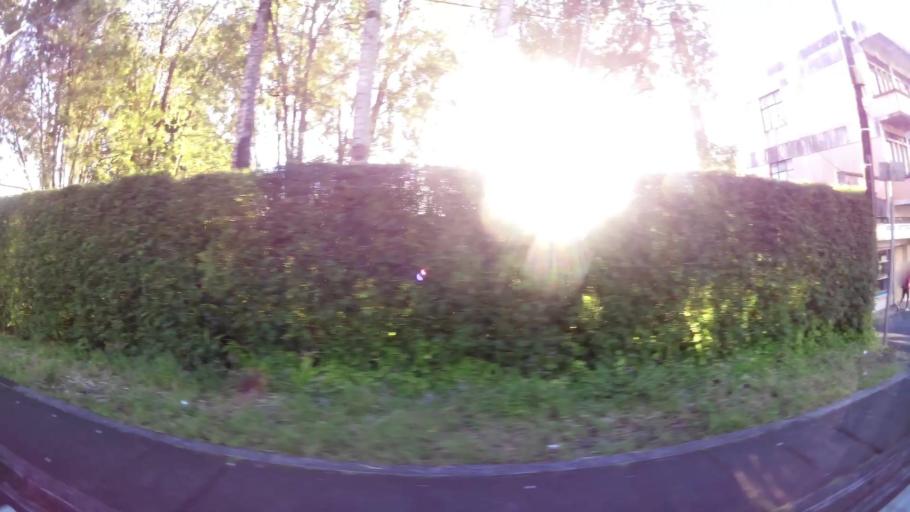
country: MU
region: Plaines Wilhems
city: Curepipe
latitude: -20.3090
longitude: 57.5249
